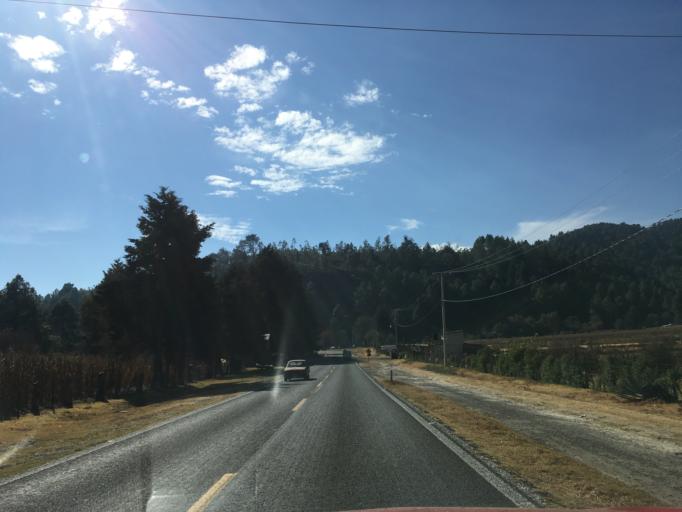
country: MX
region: Michoacan
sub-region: Hidalgo
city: Tierras Coloradas (San Pedro)
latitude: 19.7058
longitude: -100.7494
